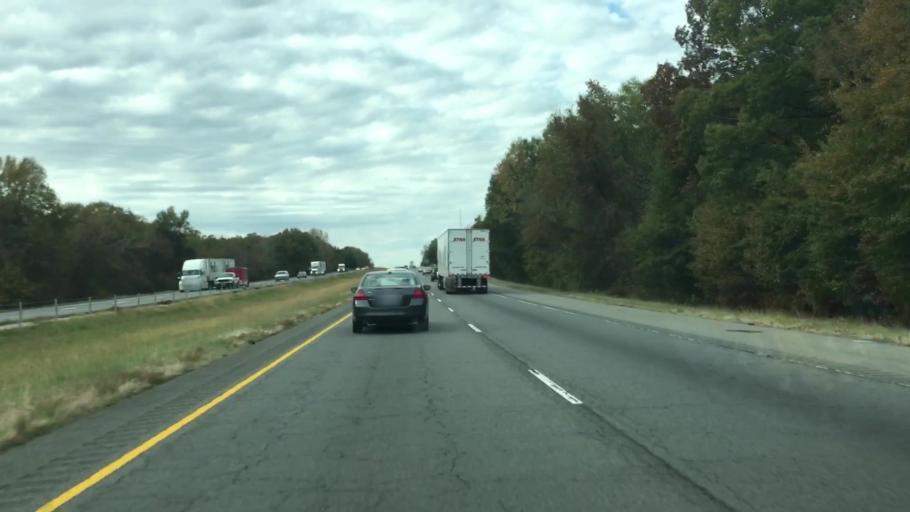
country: US
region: Arkansas
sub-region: Faulkner County
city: Conway
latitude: 35.1415
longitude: -92.5283
